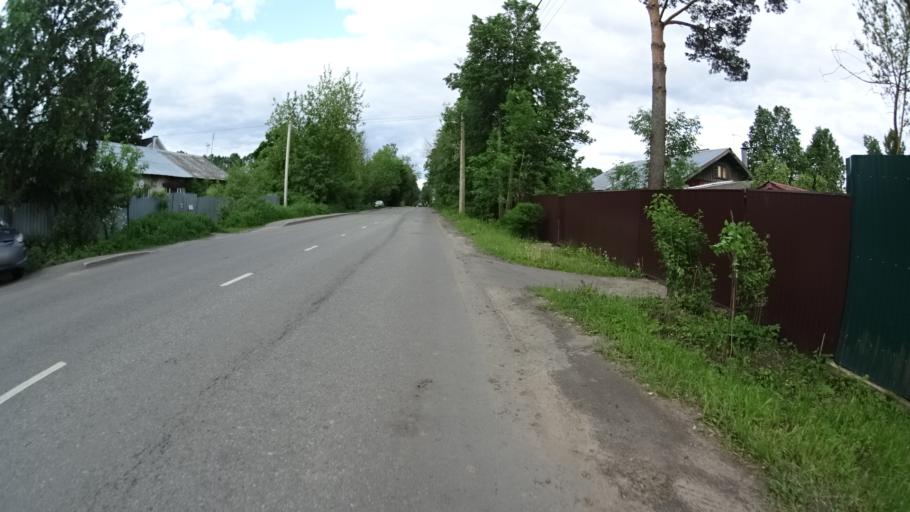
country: RU
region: Moskovskaya
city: Sofrino
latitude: 56.1298
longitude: 37.9185
